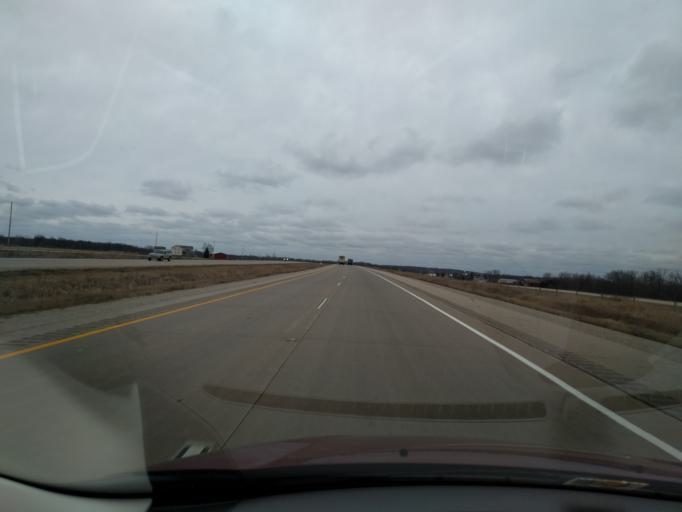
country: US
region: Wisconsin
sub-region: Winnebago County
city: Winneconne
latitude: 44.2276
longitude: -88.7126
